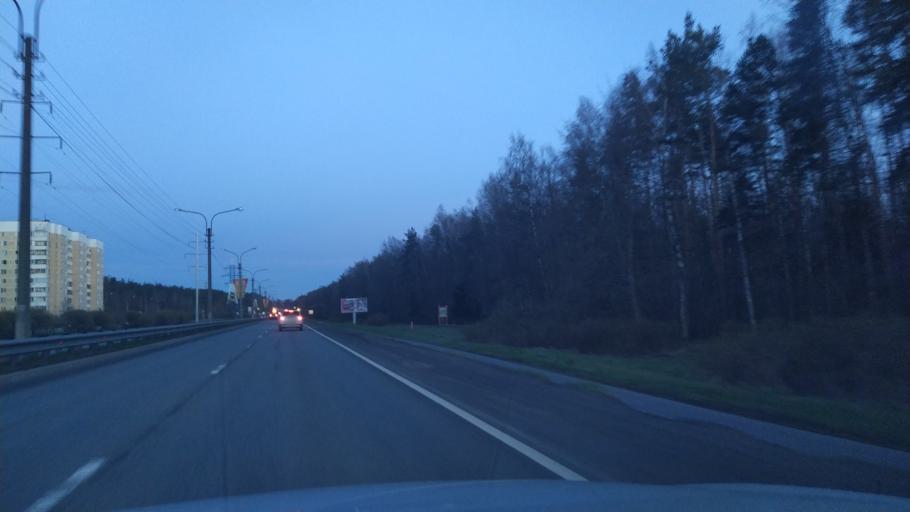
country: RU
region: St.-Petersburg
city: Razliv
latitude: 60.0788
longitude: 29.9617
